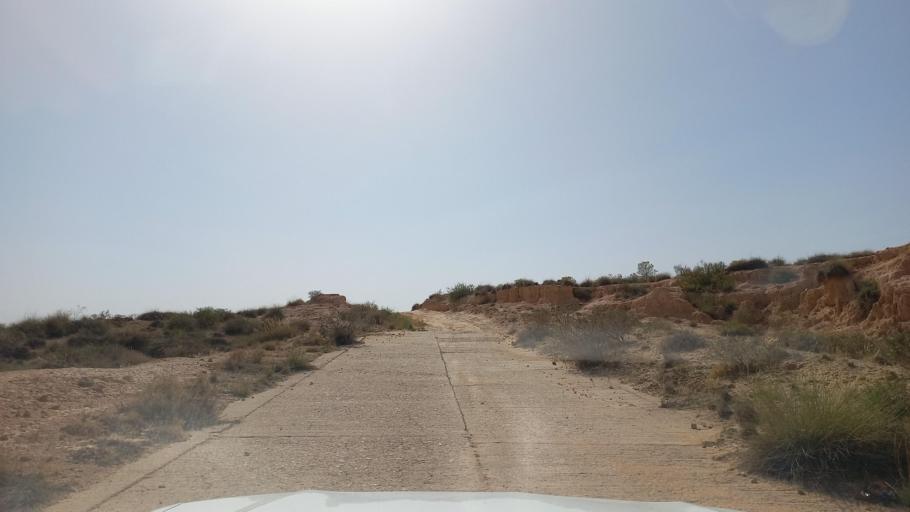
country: TN
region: Al Qasrayn
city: Kasserine
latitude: 35.2158
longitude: 9.0170
